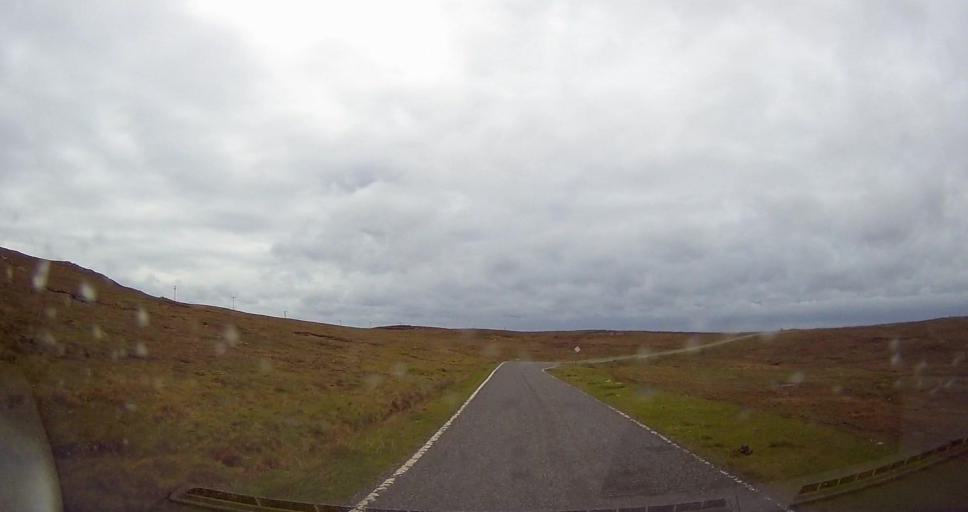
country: GB
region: Scotland
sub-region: Shetland Islands
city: Lerwick
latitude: 60.4932
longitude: -1.5703
